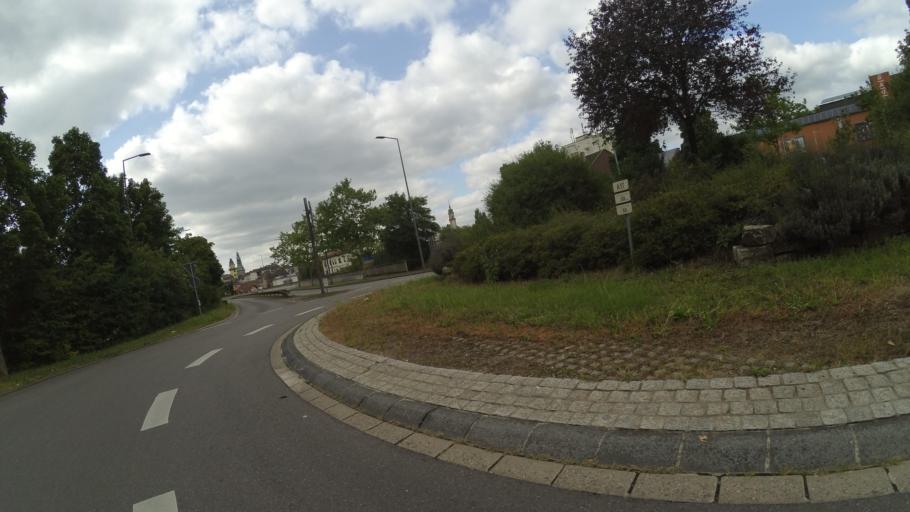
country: DE
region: Saarland
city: Volklingen
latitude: 49.2497
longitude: 6.8627
